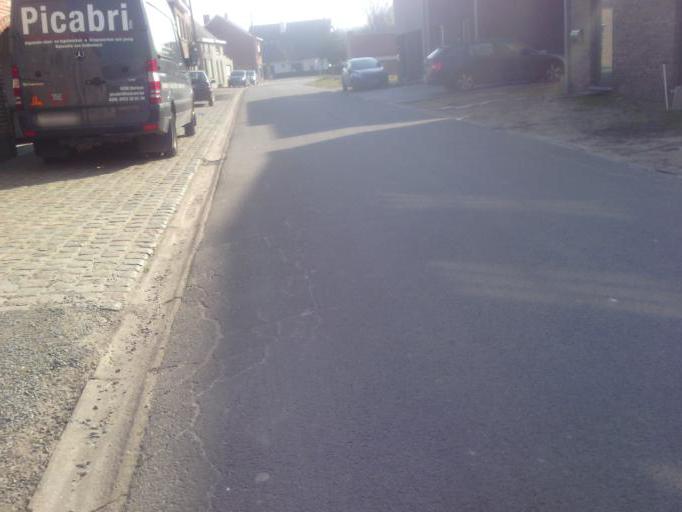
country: BE
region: Flanders
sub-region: Provincie Oost-Vlaanderen
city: Berlare
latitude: 51.0213
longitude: 3.9909
